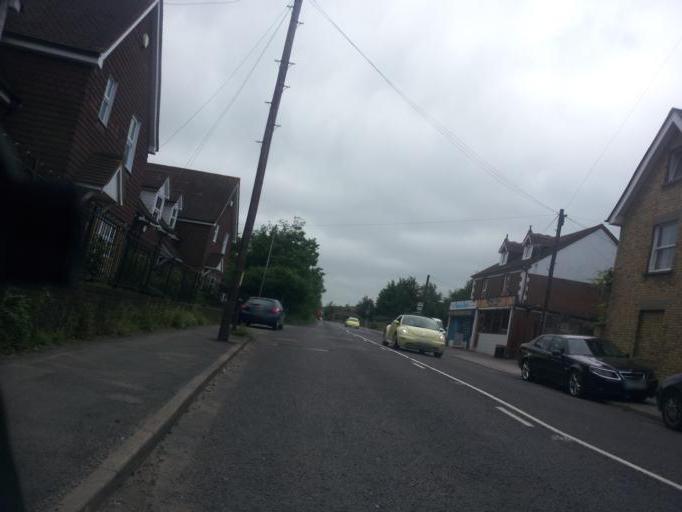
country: GB
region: England
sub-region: Kent
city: Wateringbury
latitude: 51.2495
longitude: 0.4206
